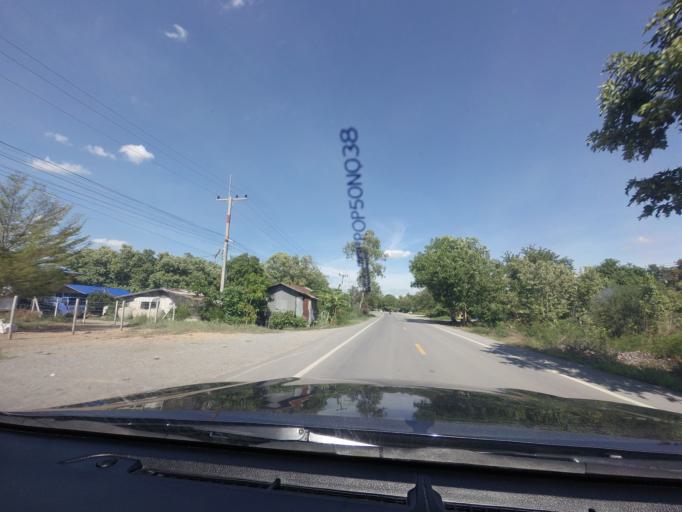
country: TH
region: Suphan Buri
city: Song Phi Nong
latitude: 14.1756
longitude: 100.0281
